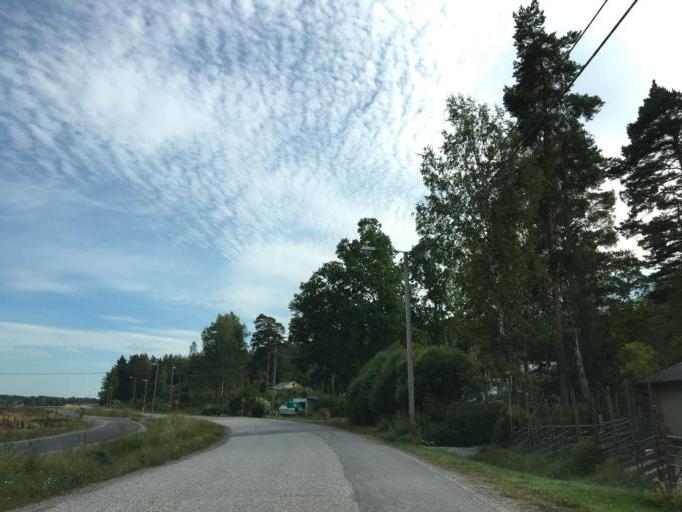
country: SE
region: Soedermanland
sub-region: Eskilstuna Kommun
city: Torshalla
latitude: 59.4515
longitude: 16.4668
